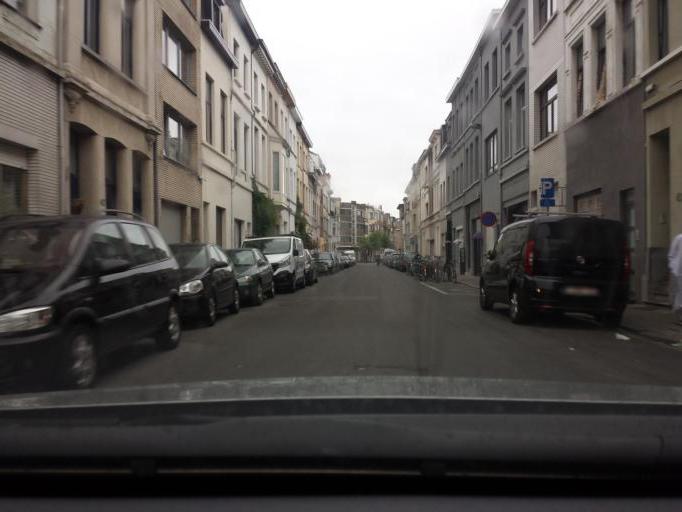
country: BE
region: Flanders
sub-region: Provincie Antwerpen
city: Antwerpen
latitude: 51.2193
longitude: 4.4378
